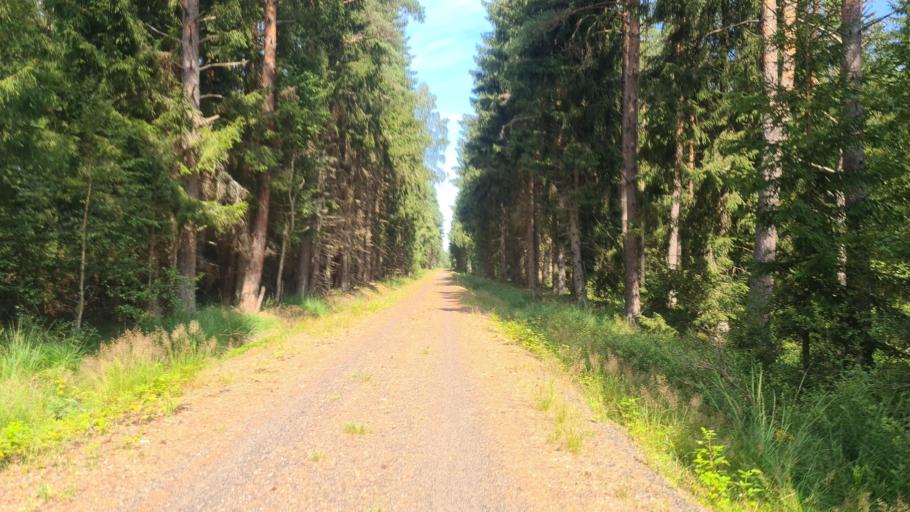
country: SE
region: Kronoberg
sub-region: Ljungby Kommun
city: Lagan
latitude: 56.9501
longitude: 13.9627
